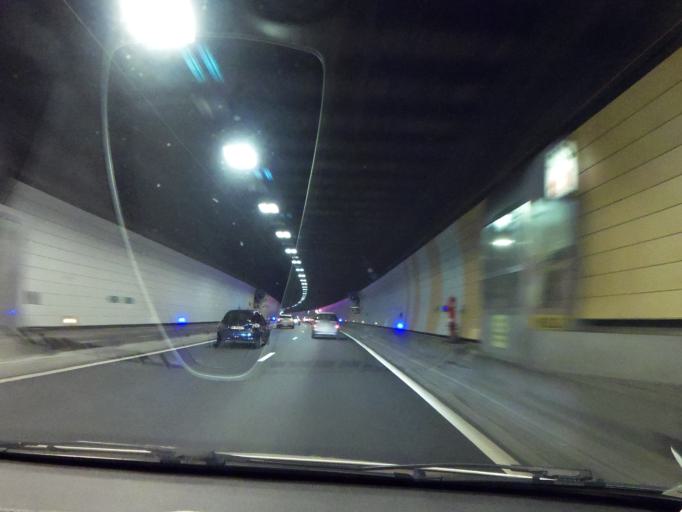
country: FR
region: Rhone-Alpes
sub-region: Departement du Rhone
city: Tassin-la-Demi-Lune
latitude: 45.7626
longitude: 4.8041
